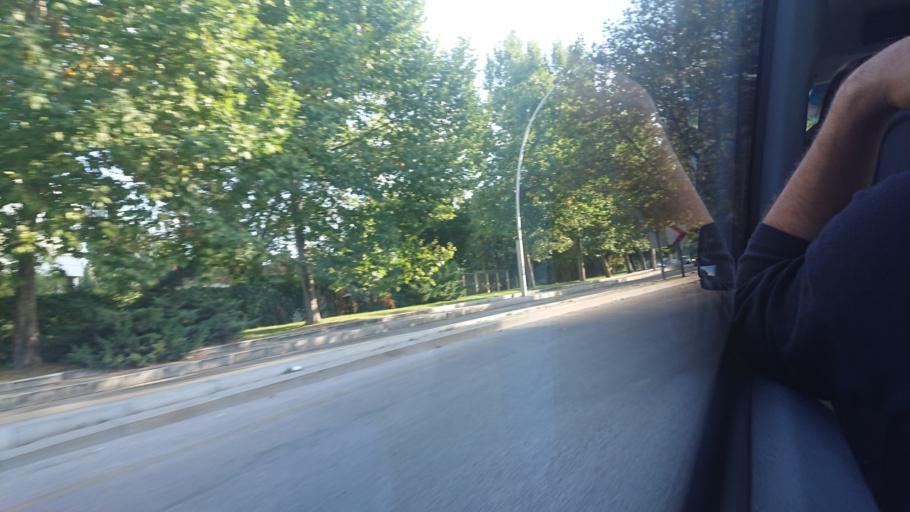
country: TR
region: Ankara
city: Ankara
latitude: 39.9123
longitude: 32.8156
